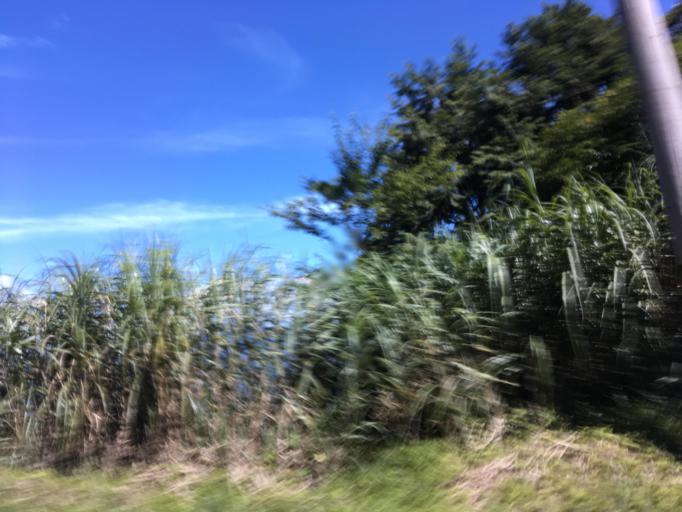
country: TW
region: Taiwan
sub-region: Yilan
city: Yilan
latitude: 24.5248
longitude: 121.5184
